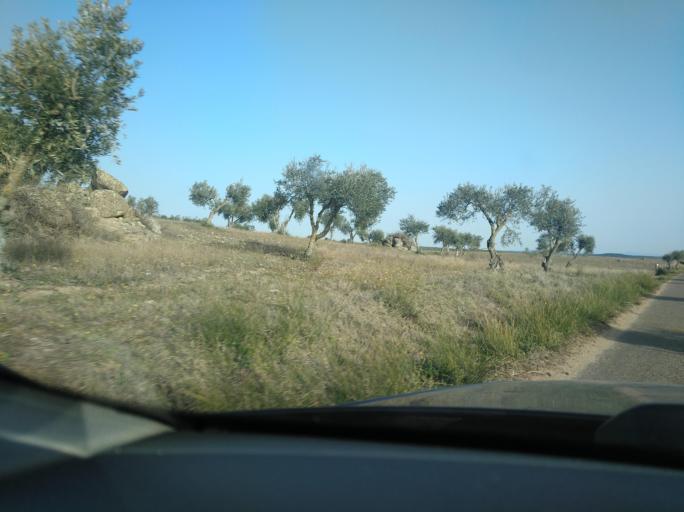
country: PT
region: Portalegre
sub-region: Campo Maior
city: Campo Maior
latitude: 39.0093
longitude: -7.0277
